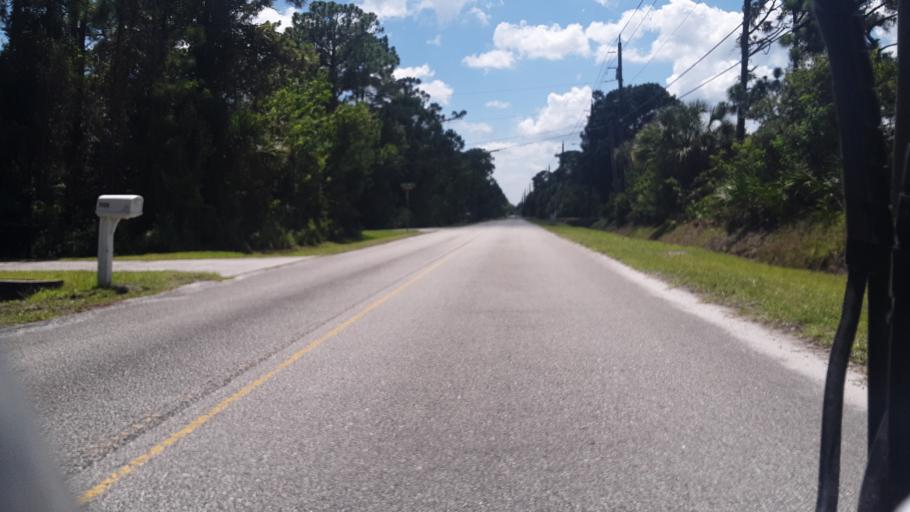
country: US
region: Florida
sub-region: Brevard County
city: Malabar
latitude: 27.9909
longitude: -80.5992
